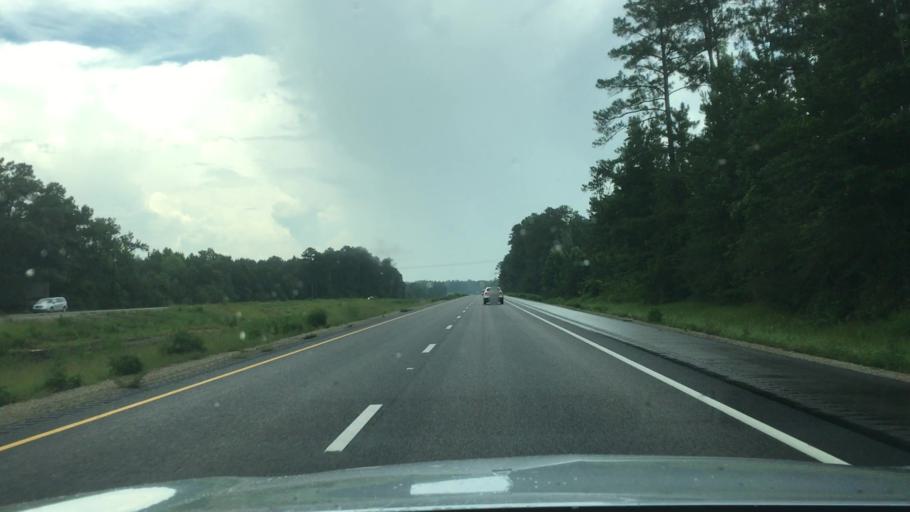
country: US
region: Mississippi
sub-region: Lamar County
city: Purvis
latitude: 31.2133
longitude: -89.3307
